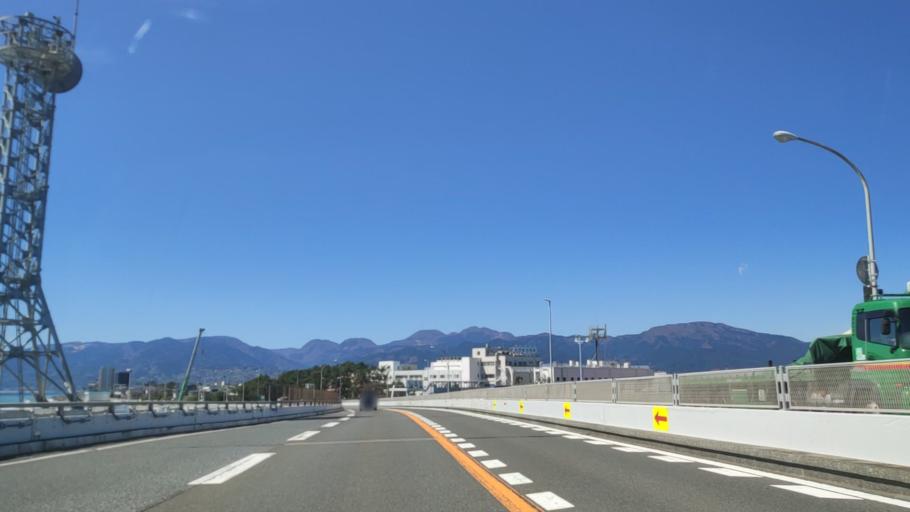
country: JP
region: Kanagawa
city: Odawara
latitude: 35.2766
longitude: 139.2064
